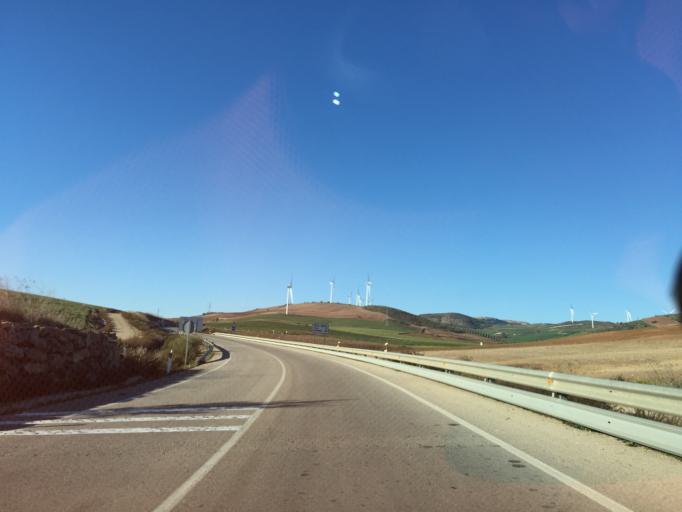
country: ES
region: Andalusia
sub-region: Provincia de Malaga
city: Ardales
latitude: 36.9388
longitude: -4.8671
